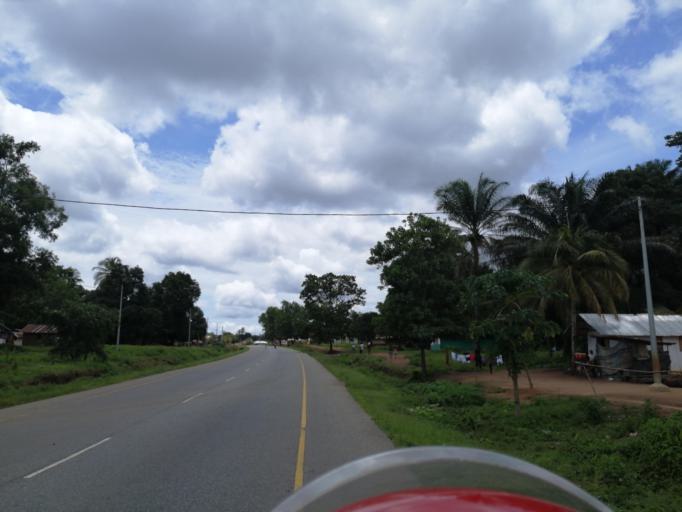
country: SL
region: Northern Province
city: Sawkta
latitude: 8.6940
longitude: -13.1095
